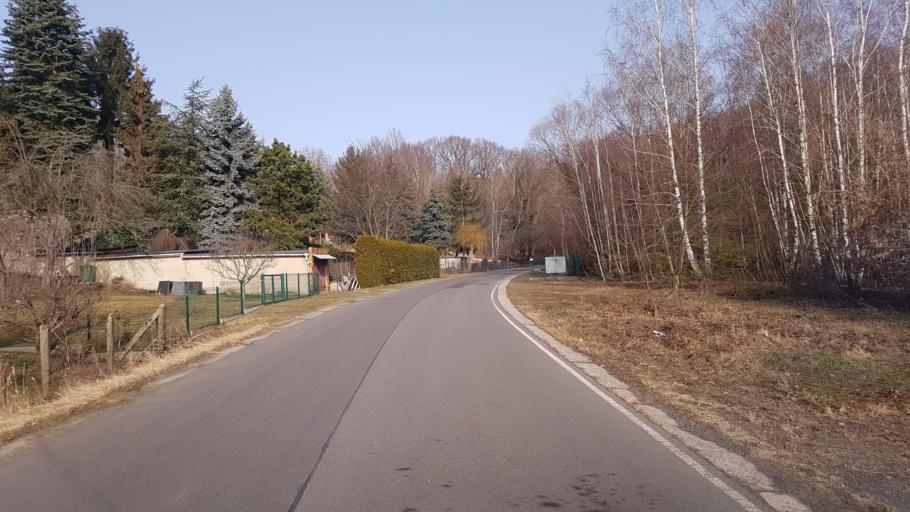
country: DE
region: Brandenburg
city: Schipkau
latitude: 51.5267
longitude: 13.8269
